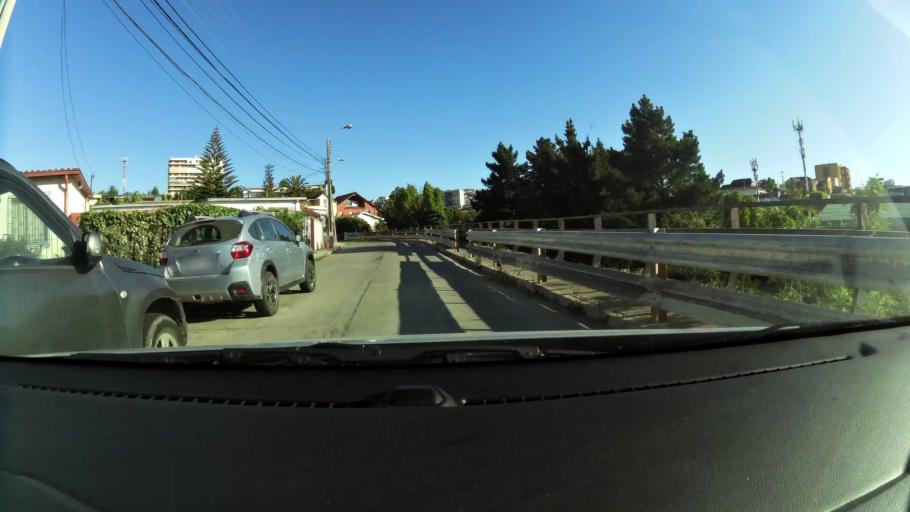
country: CL
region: Valparaiso
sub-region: Provincia de Valparaiso
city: Vina del Mar
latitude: -33.0307
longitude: -71.5837
